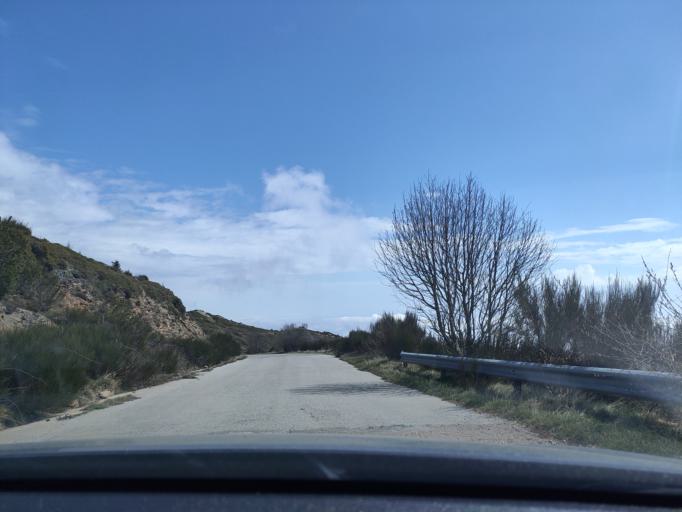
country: ES
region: Catalonia
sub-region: Provincia de Barcelona
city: Fogars de Montclus
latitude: 41.7690
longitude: 2.4458
